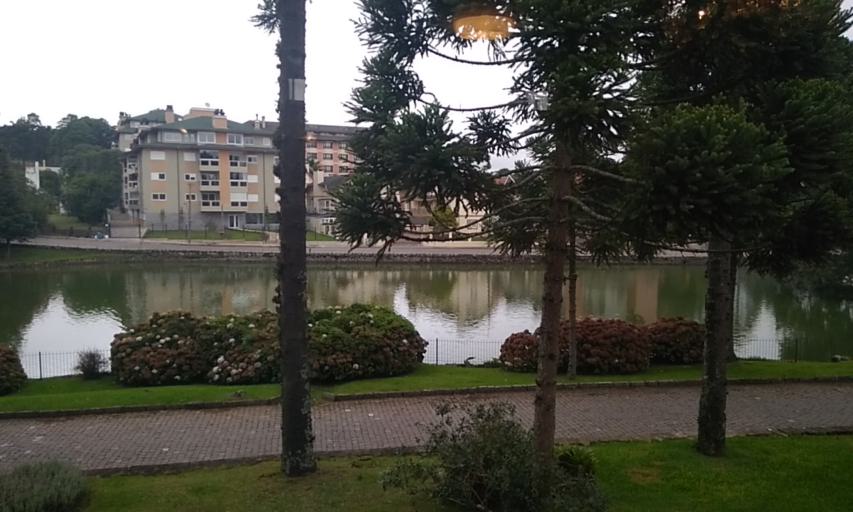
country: BR
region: Rio Grande do Sul
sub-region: Canela
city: Canela
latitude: -29.3603
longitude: -50.8190
